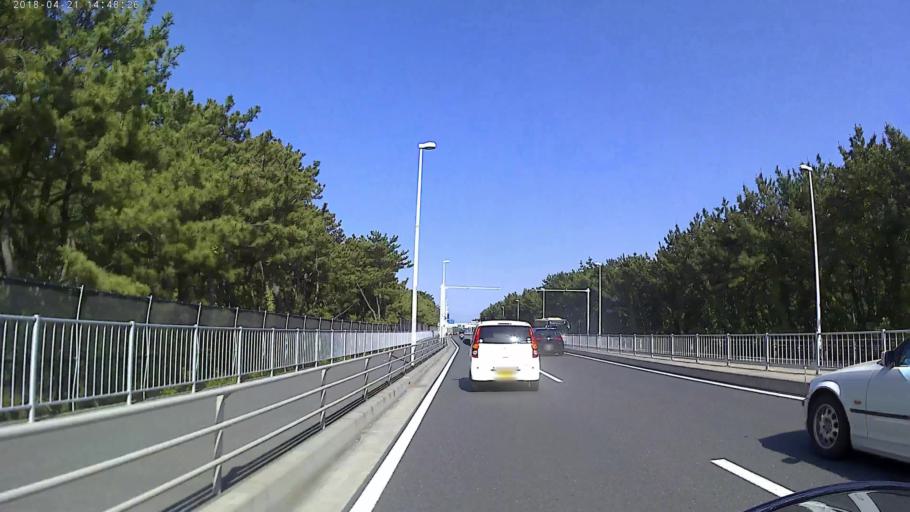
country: JP
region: Kanagawa
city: Hiratsuka
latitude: 35.3160
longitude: 139.3504
